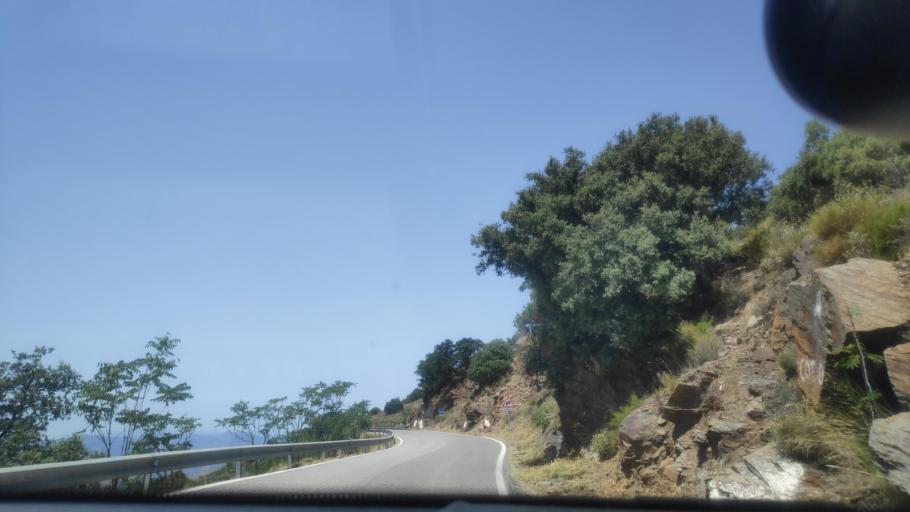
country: ES
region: Andalusia
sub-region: Provincia de Granada
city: Pampaneira
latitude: 36.9265
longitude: -3.3596
